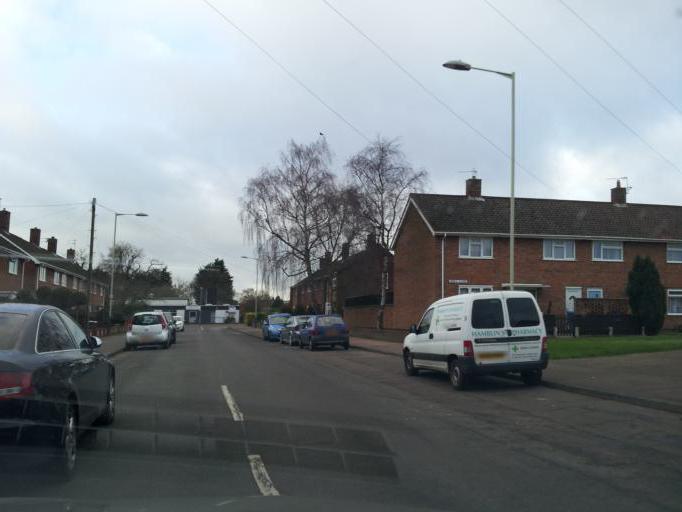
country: GB
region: England
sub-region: Norfolk
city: Thorpe Hamlet
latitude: 52.6430
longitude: 1.3356
